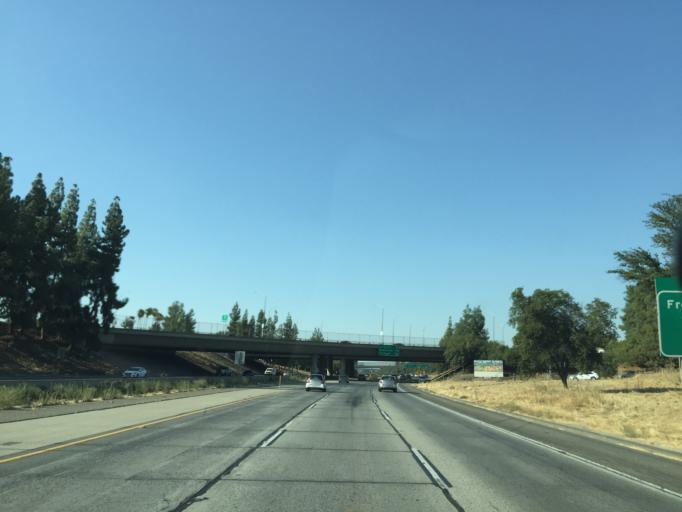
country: US
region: California
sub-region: Fresno County
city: Fresno
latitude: 36.7413
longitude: -119.7774
